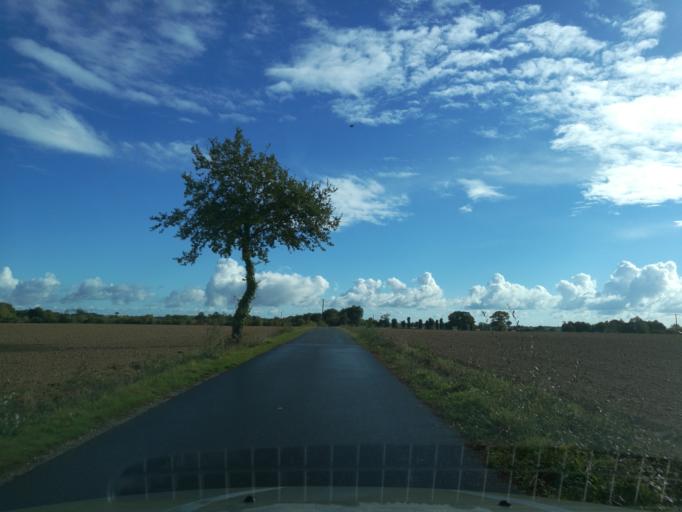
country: FR
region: Brittany
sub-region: Departement d'Ille-et-Vilaine
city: Pleumeleuc
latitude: 48.2045
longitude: -1.9261
